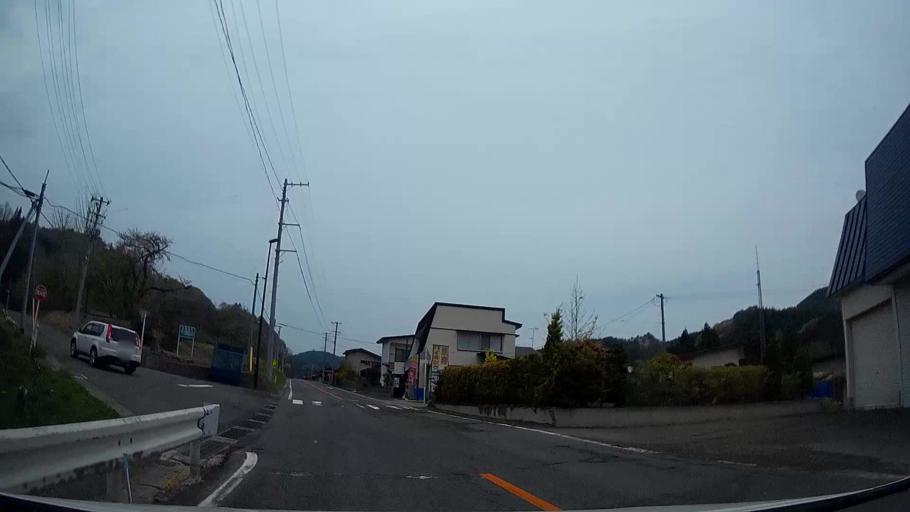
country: JP
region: Akita
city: Hanawa
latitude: 40.3013
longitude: 140.8403
